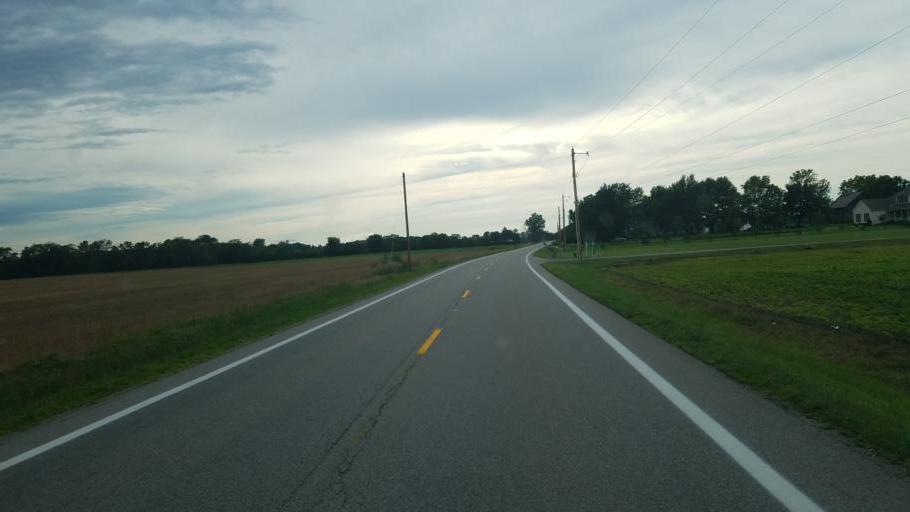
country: US
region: Ohio
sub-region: Delaware County
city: Ashley
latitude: 40.4106
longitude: -82.9887
